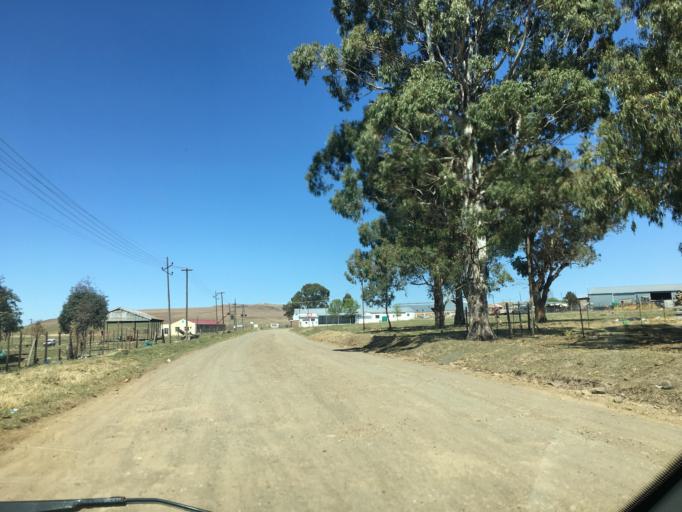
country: ZA
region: Eastern Cape
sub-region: Chris Hani District Municipality
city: Elliot
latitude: -31.3376
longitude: 27.8403
